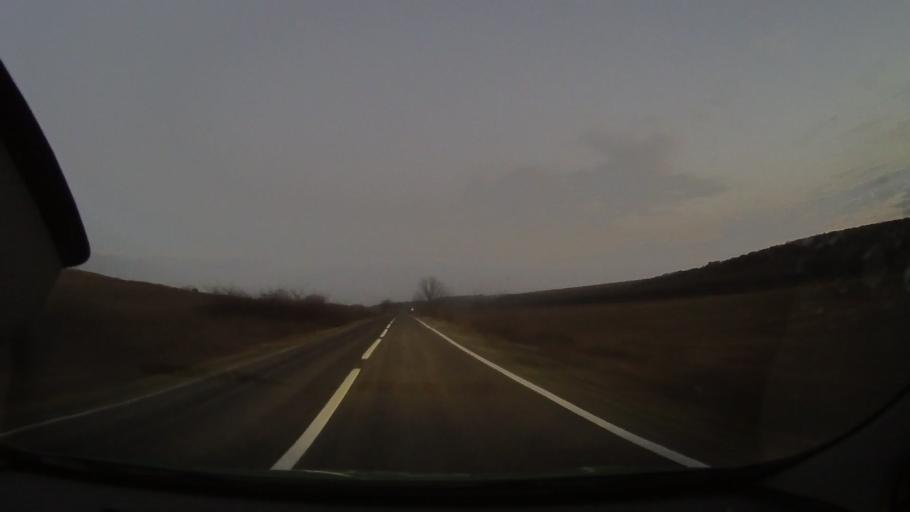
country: RO
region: Constanta
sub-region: Comuna Ion Corvin
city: Ion Corvin
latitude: 44.1054
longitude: 27.7819
